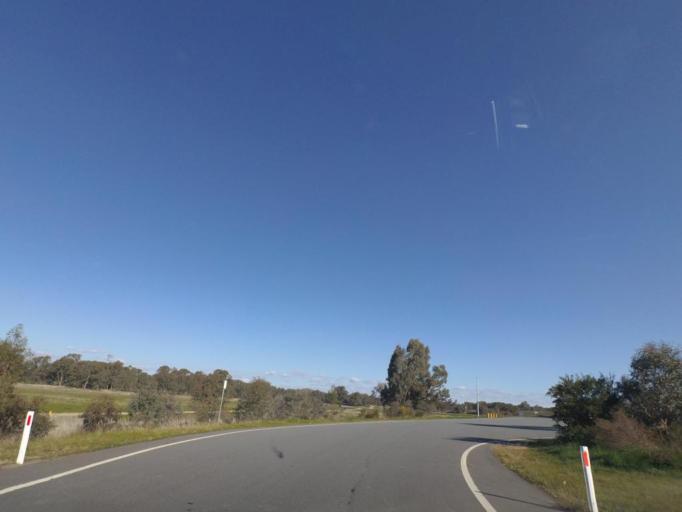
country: AU
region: Victoria
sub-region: Wangaratta
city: Wangaratta
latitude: -36.4232
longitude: 146.2637
